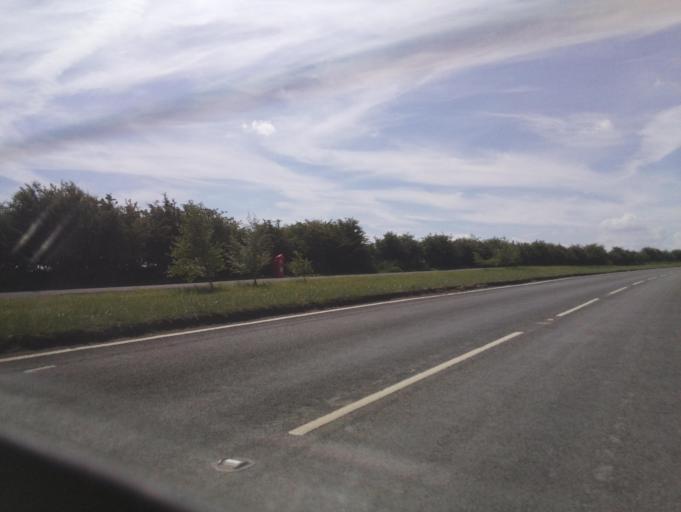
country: GB
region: England
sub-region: North Lincolnshire
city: Manton
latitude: 53.5145
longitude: -0.5799
